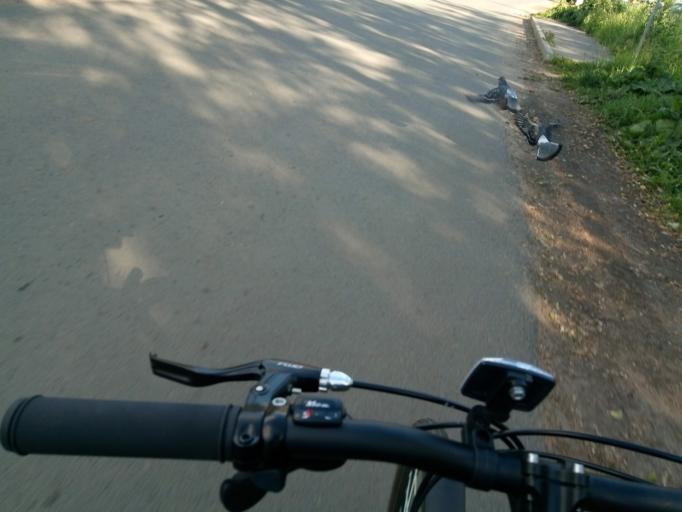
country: RU
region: Jaroslavl
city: Yaroslavl
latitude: 57.6412
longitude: 39.9145
